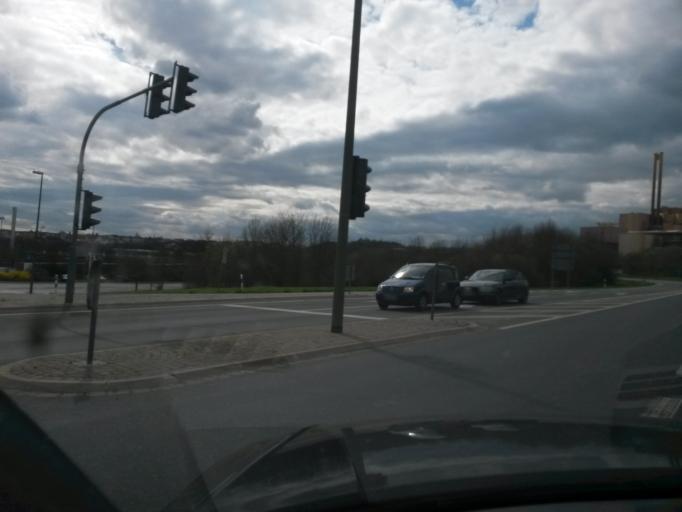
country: DE
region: Bavaria
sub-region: Regierungsbezirk Unterfranken
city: Gerbrunn
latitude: 49.7923
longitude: 10.0008
